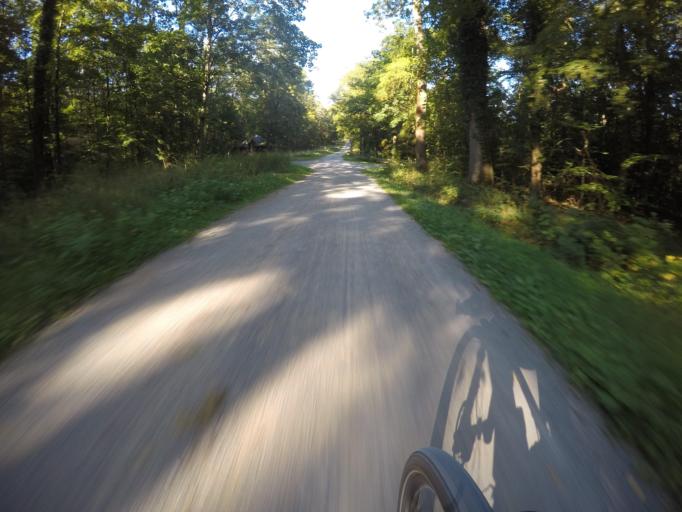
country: DE
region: Baden-Wuerttemberg
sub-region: Regierungsbezirk Stuttgart
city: Korntal
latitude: 48.7938
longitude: 9.1172
